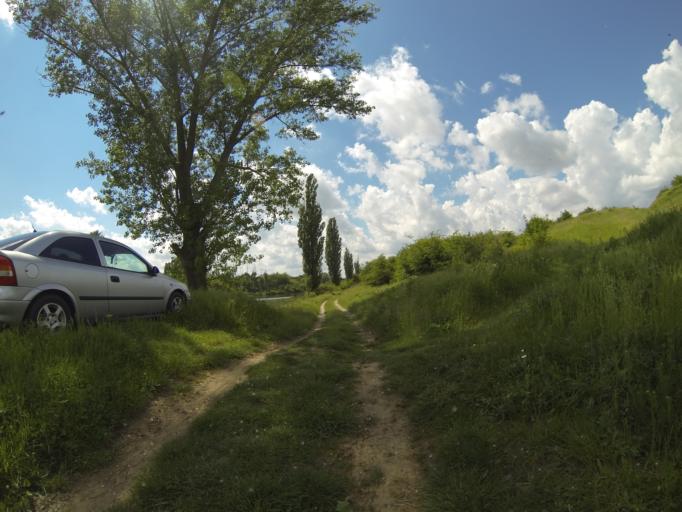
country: RO
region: Dolj
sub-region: Comuna Malu Mare
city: Preajba
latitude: 44.2652
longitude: 23.8593
